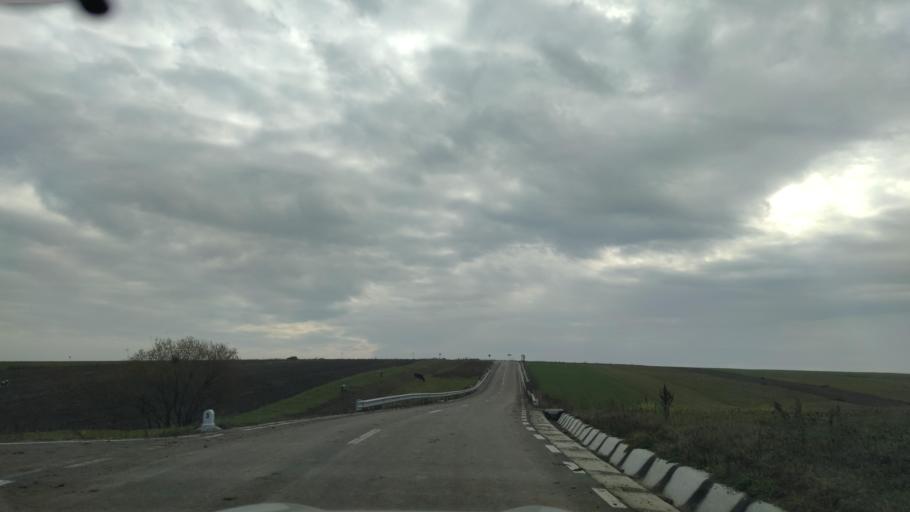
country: RO
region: Harghita
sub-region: Comuna Subcetate
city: Subcetate
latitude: 46.8201
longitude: 25.4475
